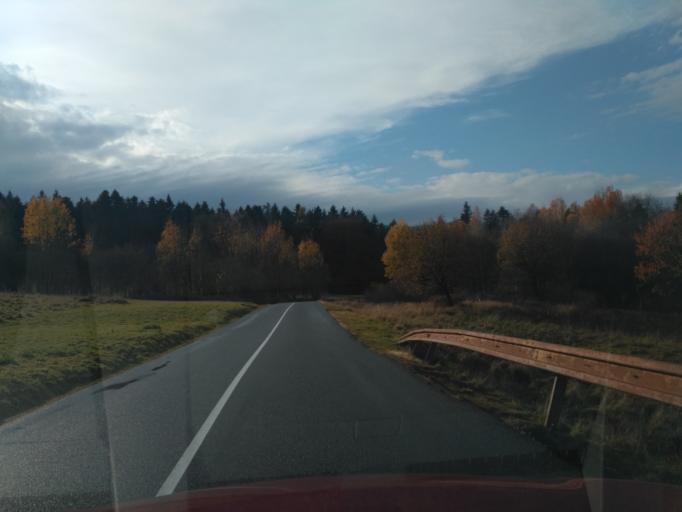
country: SK
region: Kosicky
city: Medzev
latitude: 48.7898
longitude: 20.7730
